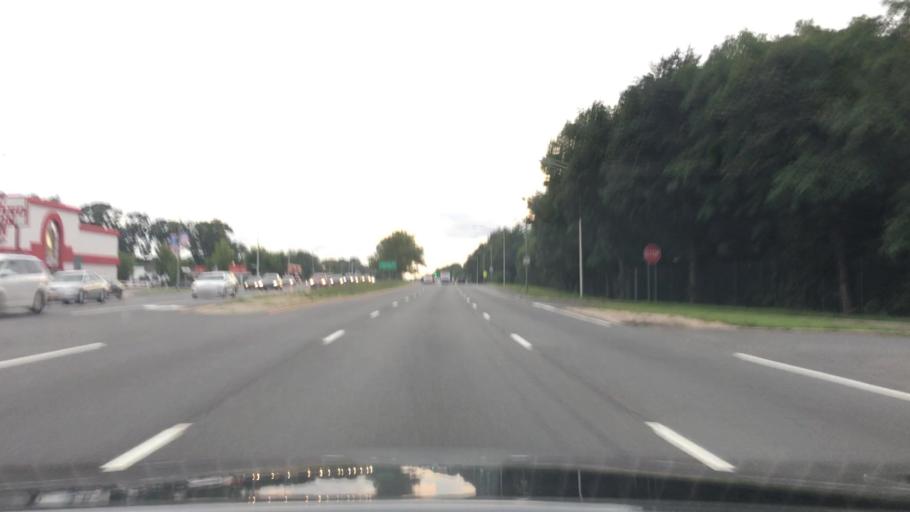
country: US
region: New York
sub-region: Nassau County
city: Bellmore
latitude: 40.6674
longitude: -73.5334
